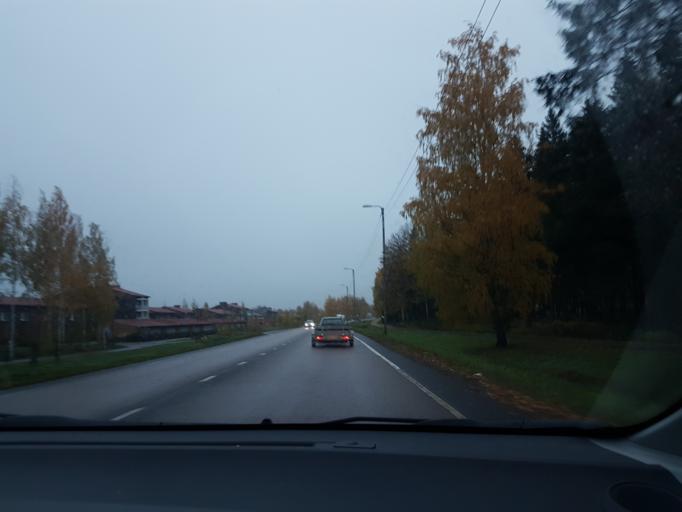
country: FI
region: Uusimaa
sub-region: Helsinki
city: Tuusula
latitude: 60.4061
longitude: 25.0366
